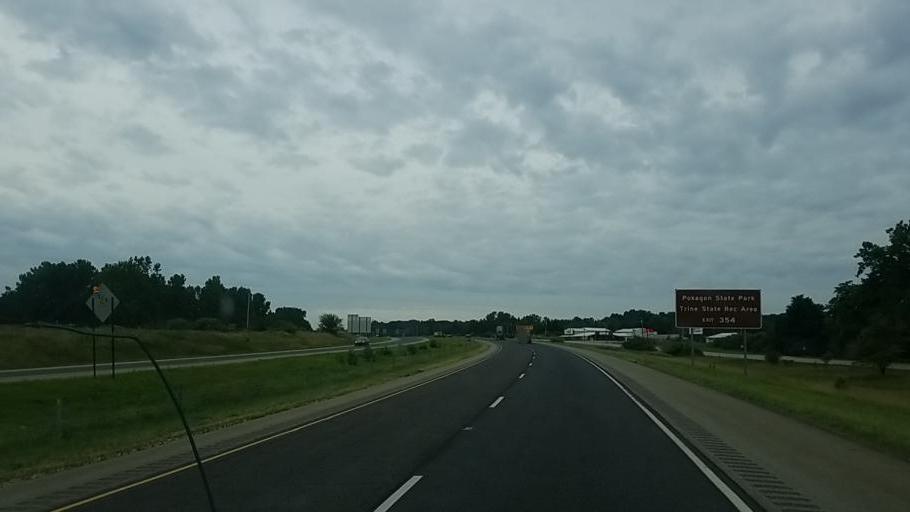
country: US
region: Indiana
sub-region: Steuben County
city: Fremont
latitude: 41.7167
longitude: -85.0035
